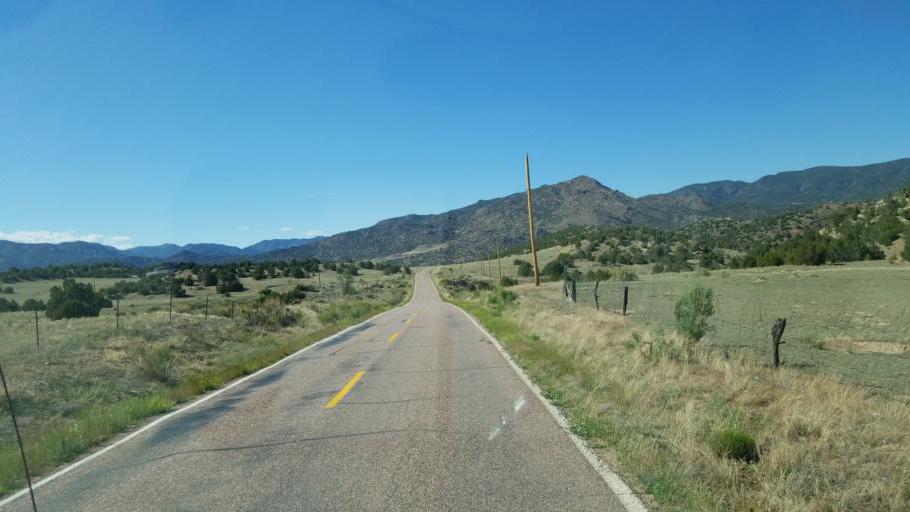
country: US
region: Colorado
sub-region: Fremont County
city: Canon City
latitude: 38.4661
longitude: -105.3770
